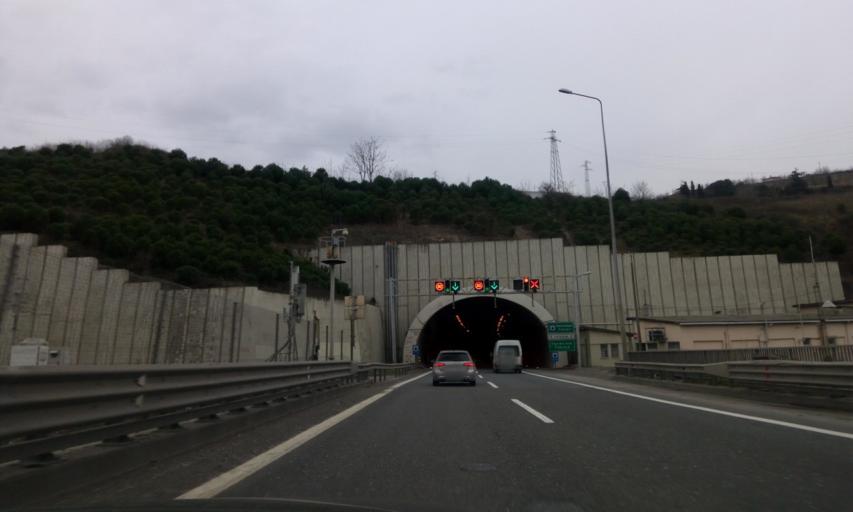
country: TR
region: Kocaeli
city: Izmit
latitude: 40.7755
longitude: 29.9006
